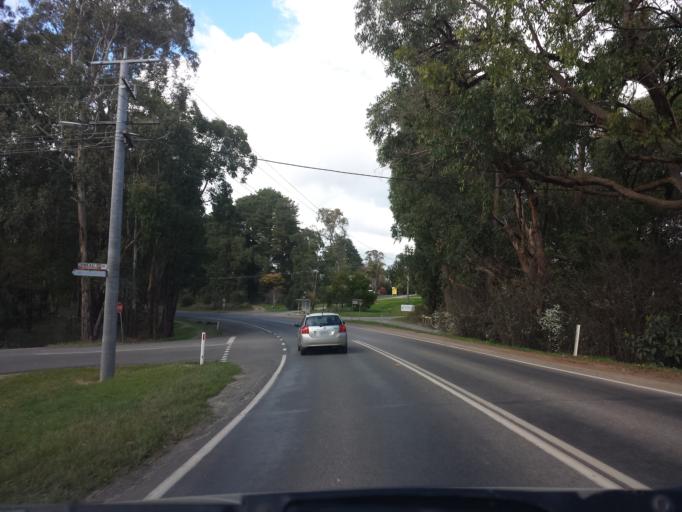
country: AU
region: Victoria
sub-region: Yarra Ranges
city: Mount Evelyn
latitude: -37.7959
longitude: 145.3894
